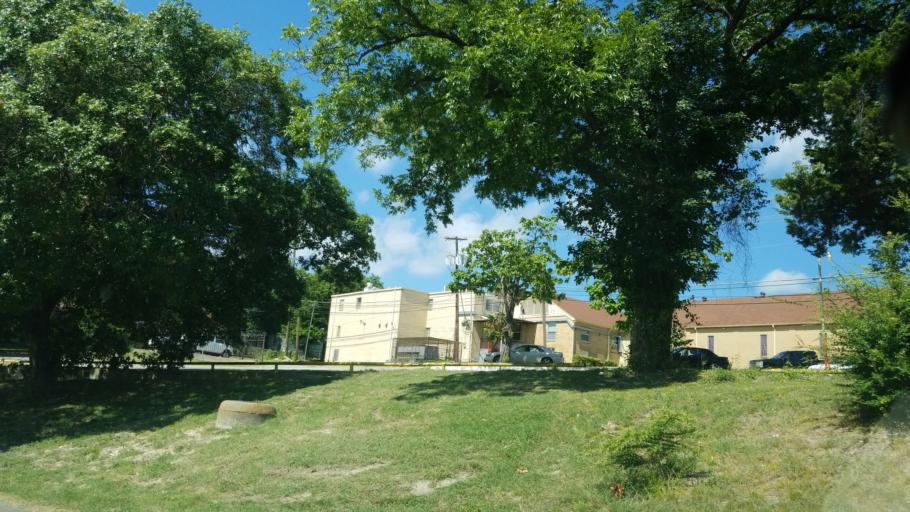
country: US
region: Texas
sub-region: Dallas County
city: Dallas
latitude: 32.7305
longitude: -96.7939
